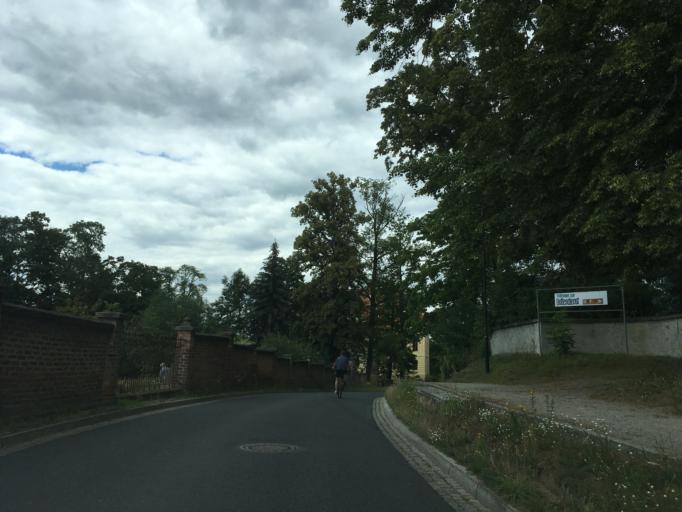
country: DE
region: Saxony
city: Wachau
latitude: 51.1577
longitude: 13.9039
